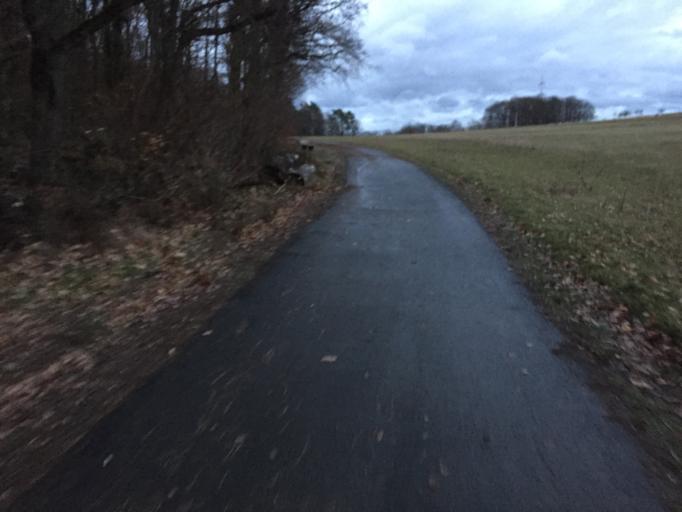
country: DE
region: Hesse
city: Allendorf an der Lahn
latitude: 50.5609
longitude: 8.6245
